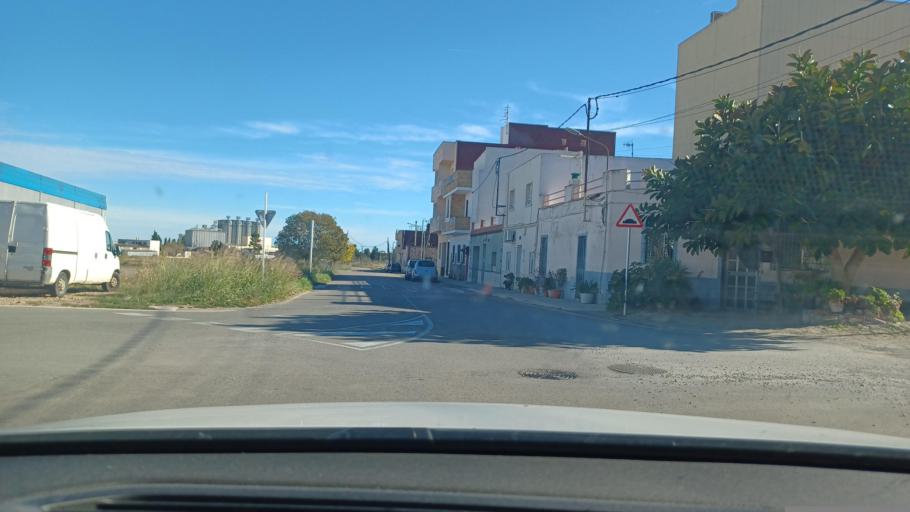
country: ES
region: Catalonia
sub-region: Provincia de Tarragona
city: Amposta
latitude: 40.7008
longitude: 0.5686
